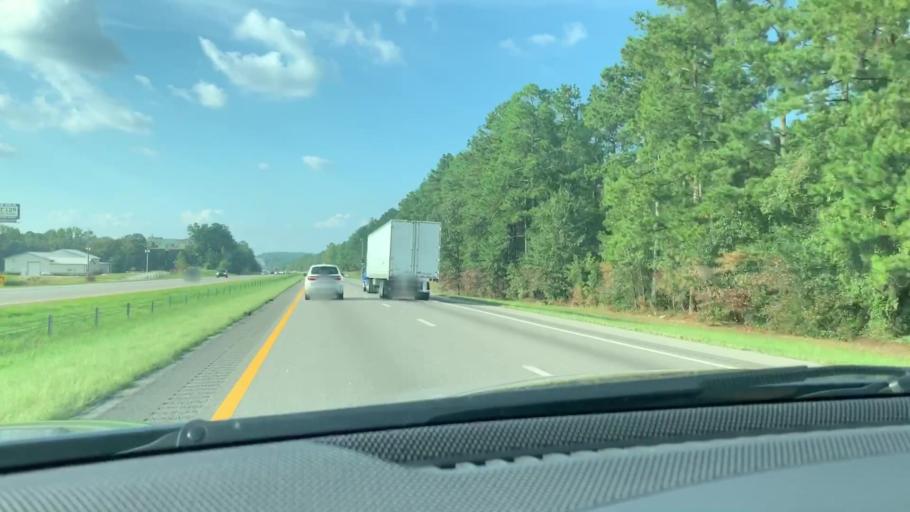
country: US
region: South Carolina
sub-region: Calhoun County
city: Oak Grove
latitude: 33.7075
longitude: -80.9186
